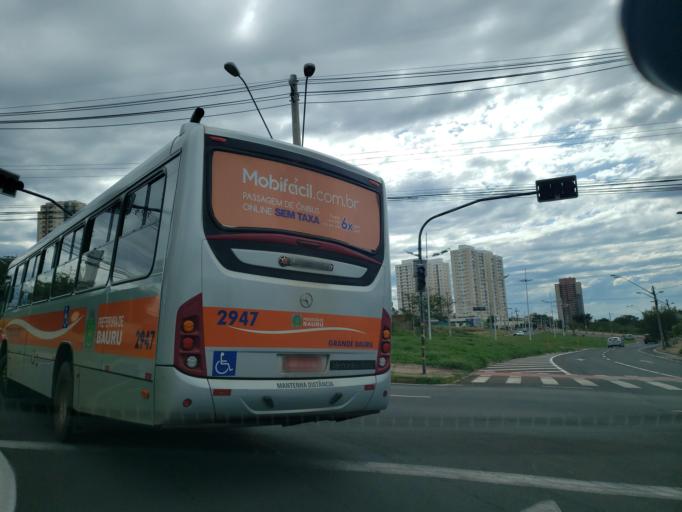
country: BR
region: Sao Paulo
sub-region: Bauru
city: Bauru
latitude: -22.3377
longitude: -49.0408
